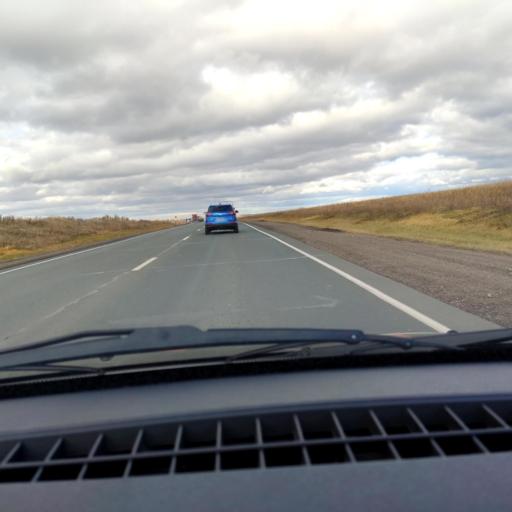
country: RU
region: Bashkortostan
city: Avdon
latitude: 54.7129
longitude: 55.7757
